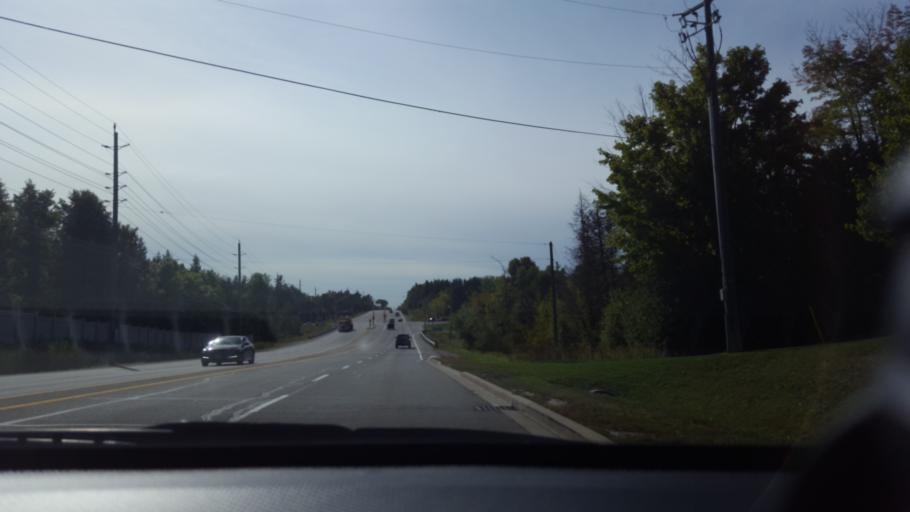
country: CA
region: Ontario
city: Newmarket
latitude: 43.9962
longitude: -79.4949
